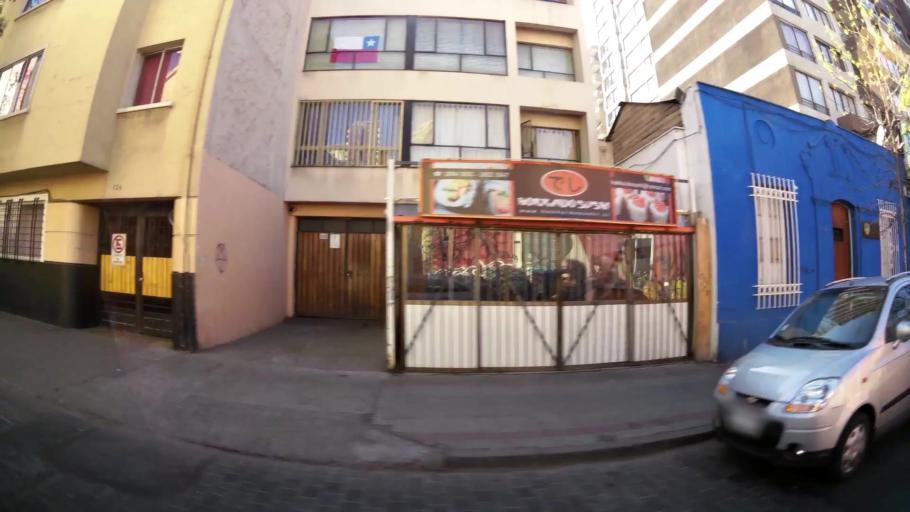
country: CL
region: Santiago Metropolitan
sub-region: Provincia de Santiago
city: Santiago
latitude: -33.4443
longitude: -70.6407
